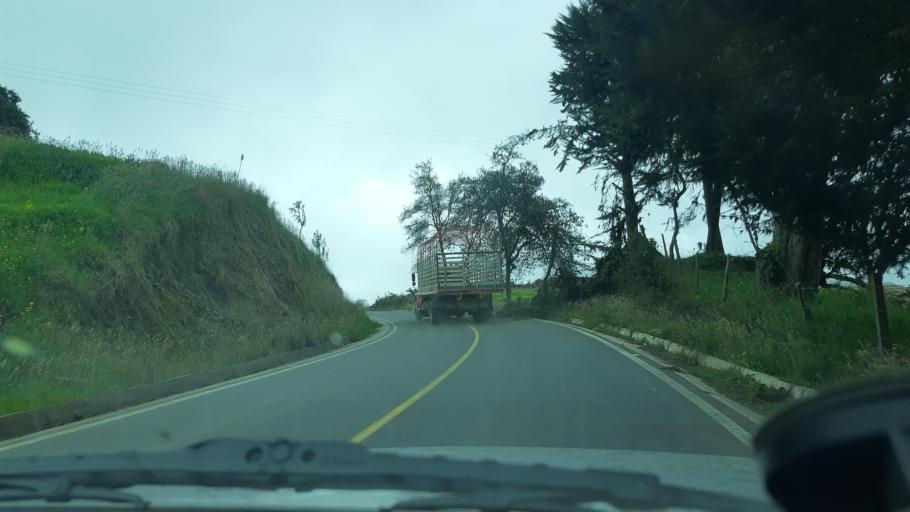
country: CO
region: Cundinamarca
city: Umbita
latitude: 5.2309
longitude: -73.4700
